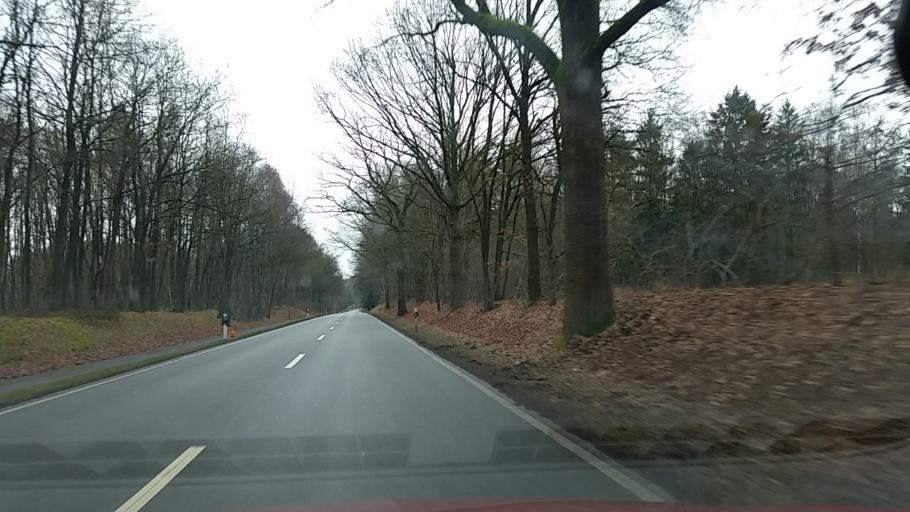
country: DE
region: Lower Saxony
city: Bispingen
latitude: 53.0699
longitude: 9.9952
